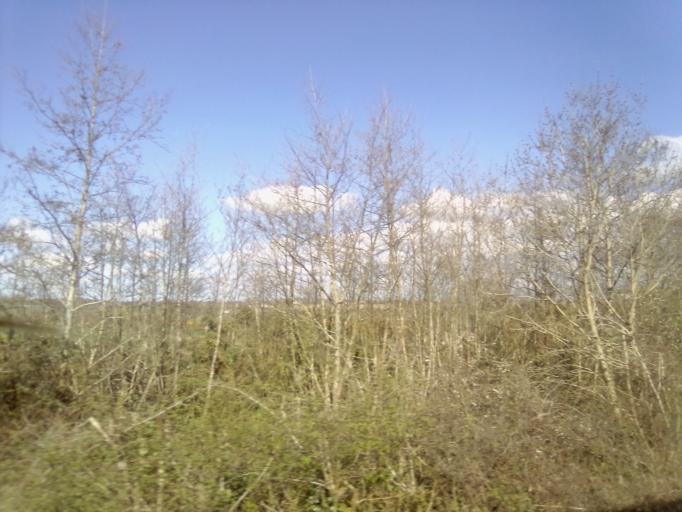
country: IE
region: Munster
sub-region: County Cork
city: Kanturk
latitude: 52.1265
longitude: -8.8208
